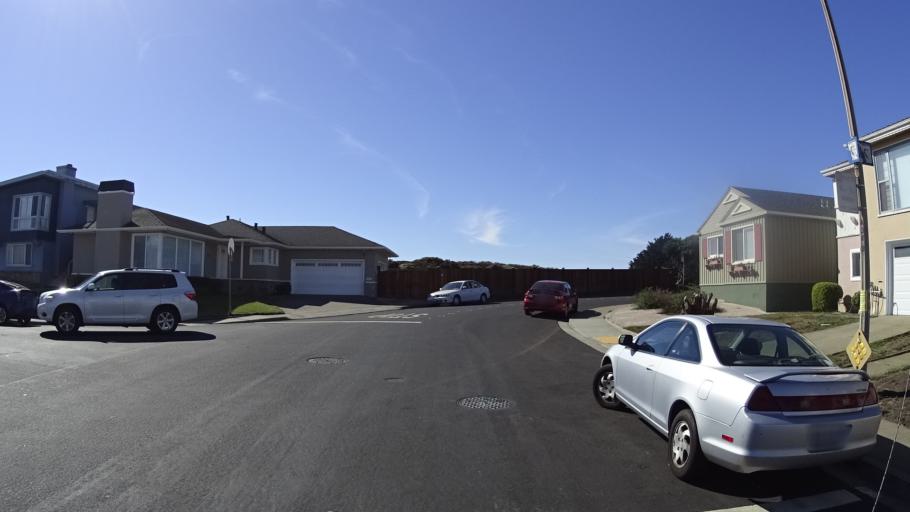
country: US
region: California
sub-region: San Mateo County
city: Broadmoor
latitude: 37.6960
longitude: -122.4939
